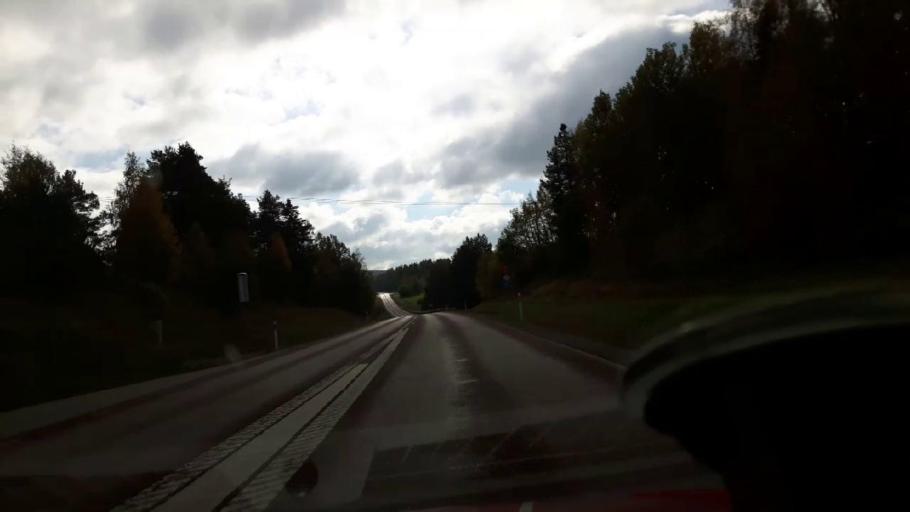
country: SE
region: Gaevleborg
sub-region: Ljusdals Kommun
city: Jaervsoe
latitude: 61.6709
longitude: 16.1460
